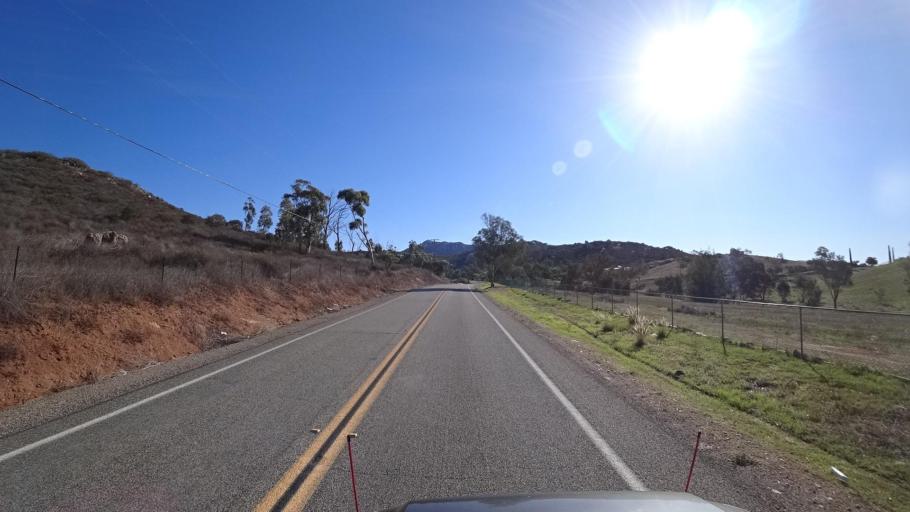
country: US
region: California
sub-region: San Diego County
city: Jamul
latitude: 32.6654
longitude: -116.7920
